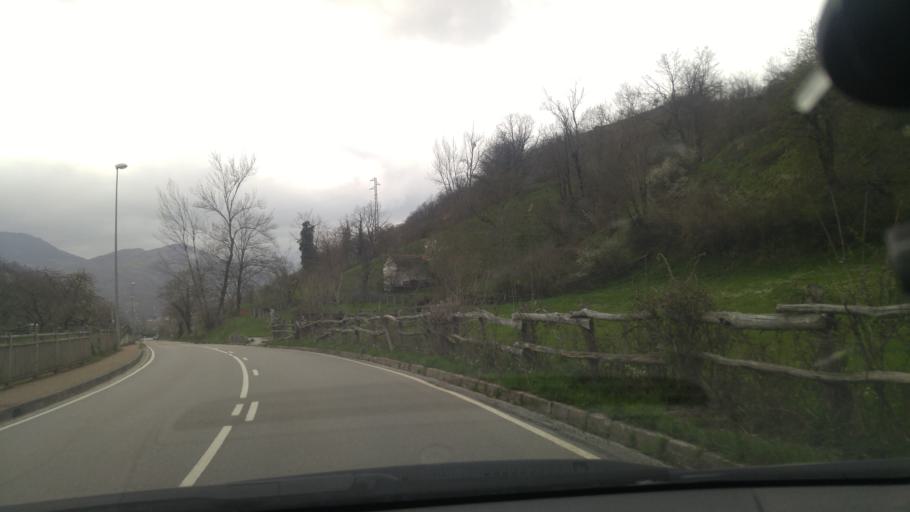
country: ES
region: Asturias
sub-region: Province of Asturias
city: Rio Aller
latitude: 43.1168
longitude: -5.5344
